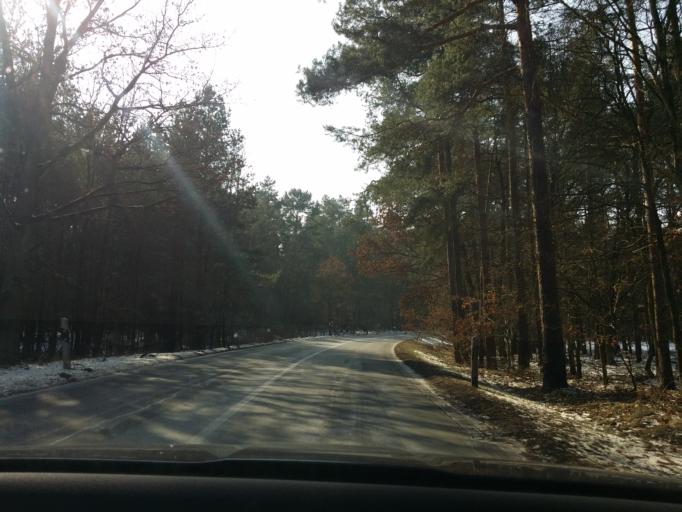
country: DE
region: Brandenburg
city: Wittstock
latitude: 53.1929
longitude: 12.5625
